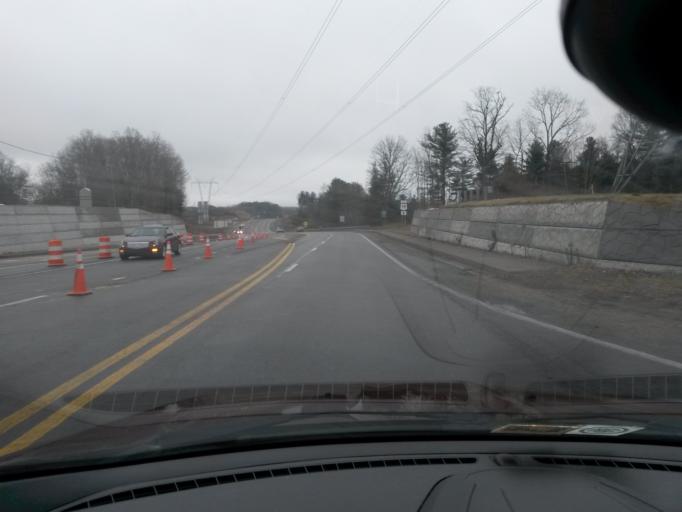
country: US
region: West Virginia
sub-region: Raleigh County
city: Beckley
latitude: 37.7972
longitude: -81.1712
